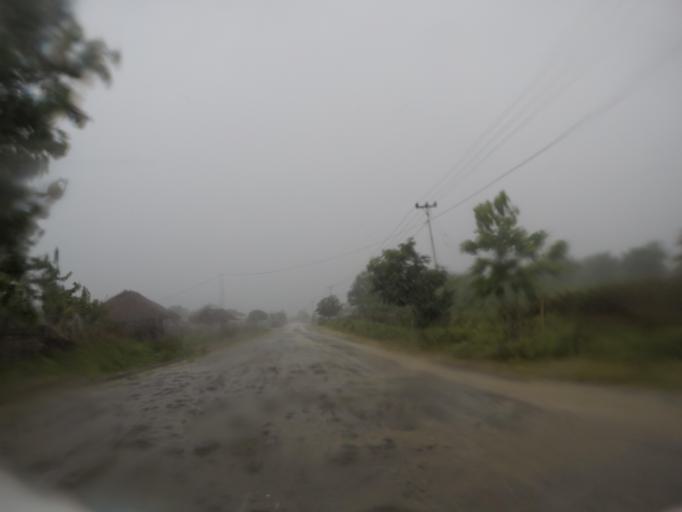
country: TL
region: Bobonaro
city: Maliana
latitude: -8.8583
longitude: 125.1009
